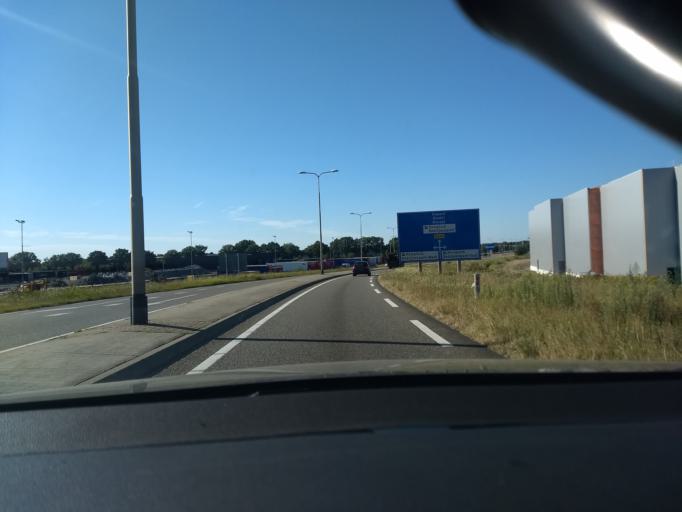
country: NL
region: North Brabant
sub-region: Gemeente Eersel
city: Eersel
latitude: 51.3523
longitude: 5.2735
